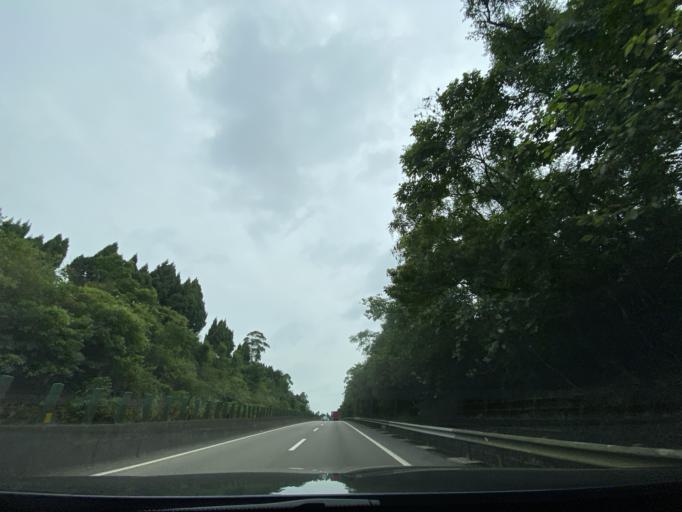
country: CN
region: Sichuan
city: Neijiang
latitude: 29.6522
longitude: 104.9842
